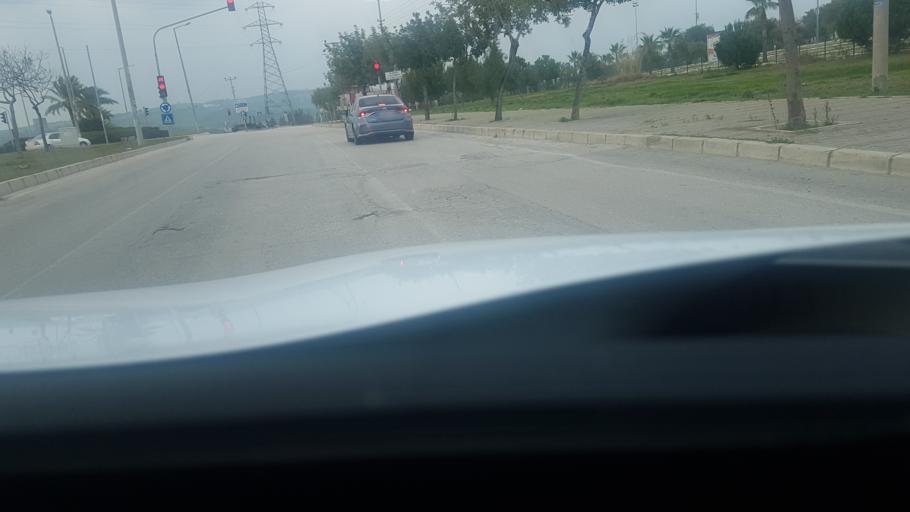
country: TR
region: Adana
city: Seyhan
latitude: 37.0568
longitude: 35.2461
